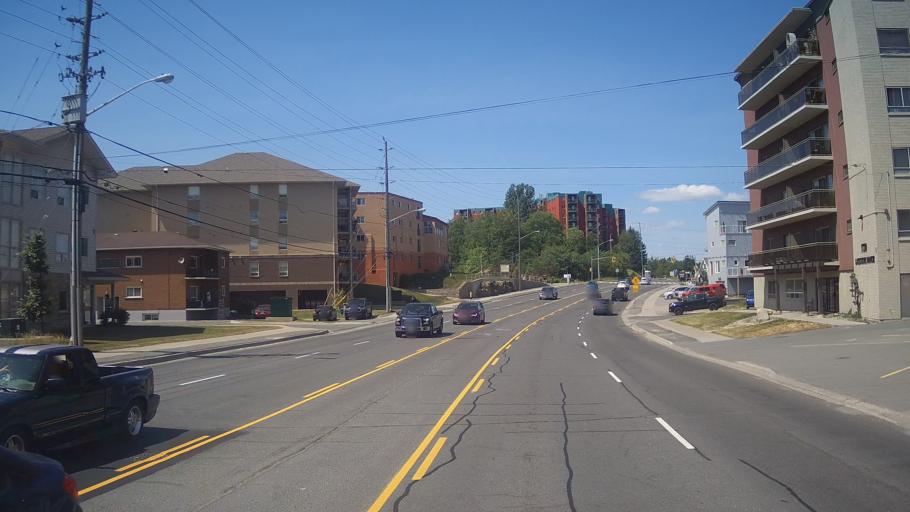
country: CA
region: Ontario
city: Greater Sudbury
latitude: 46.4569
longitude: -81.0014
